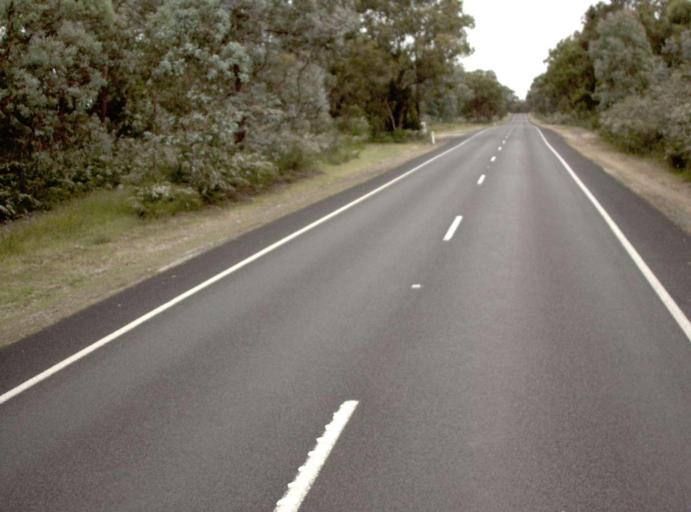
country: AU
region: Victoria
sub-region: Wellington
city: Sale
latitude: -38.3436
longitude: 147.0036
